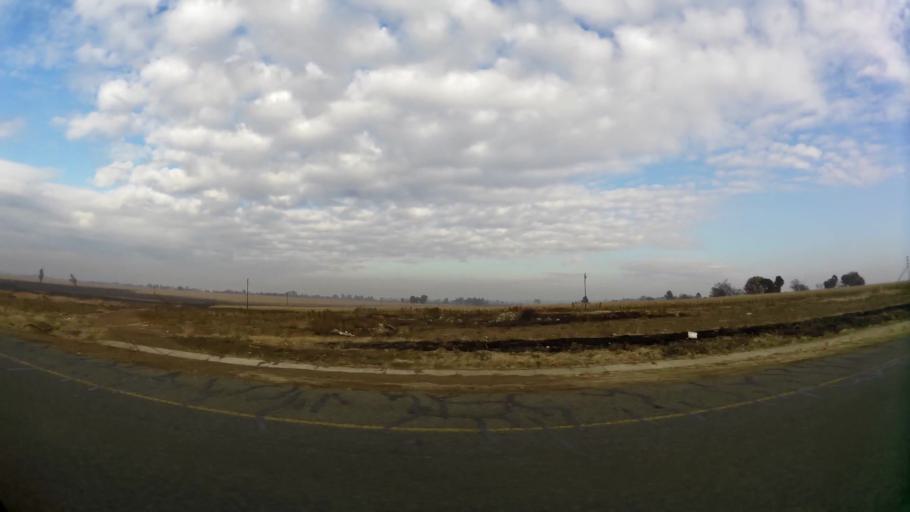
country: ZA
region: Gauteng
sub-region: Sedibeng District Municipality
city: Vanderbijlpark
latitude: -26.6499
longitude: 27.7800
